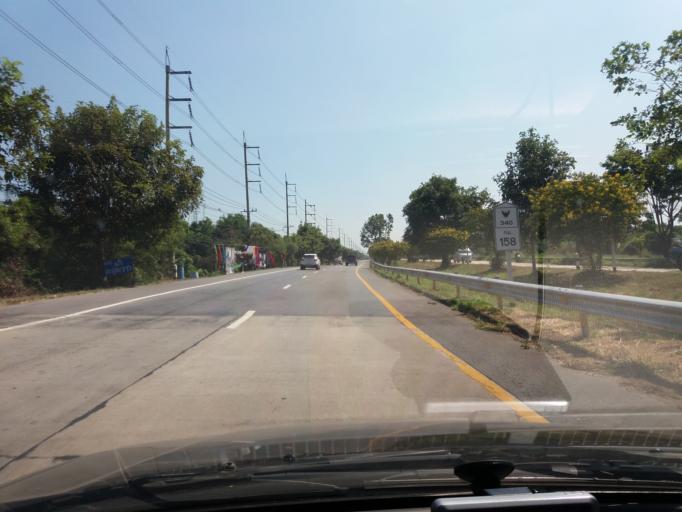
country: TH
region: Chai Nat
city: Chai Nat
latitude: 15.1400
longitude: 100.1427
